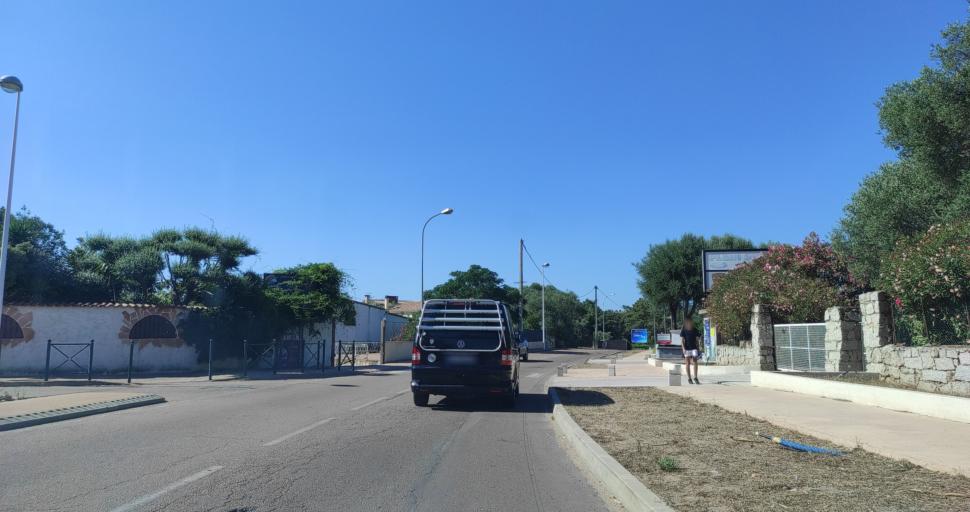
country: FR
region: Corsica
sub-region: Departement de la Corse-du-Sud
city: Porto-Vecchio
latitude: 41.5866
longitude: 9.2823
